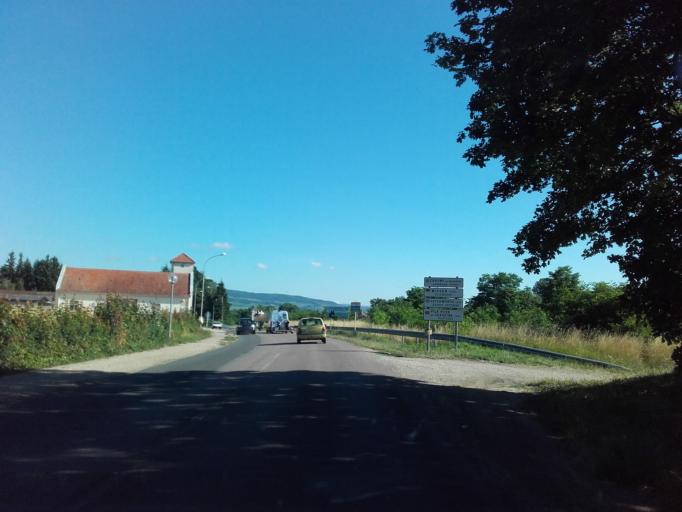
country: FR
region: Bourgogne
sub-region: Departement de Saone-et-Loire
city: Chagny
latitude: 46.8996
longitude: 4.7522
